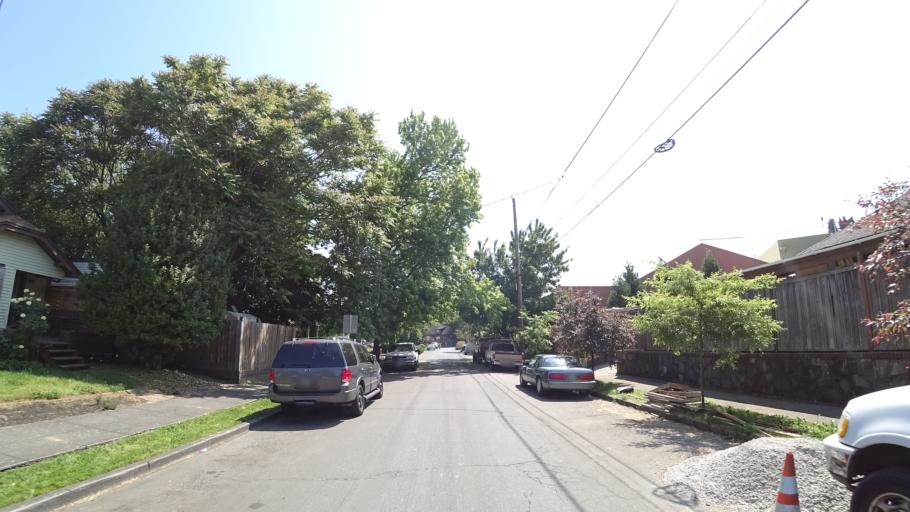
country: US
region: Oregon
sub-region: Multnomah County
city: Portland
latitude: 45.5732
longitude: -122.6582
